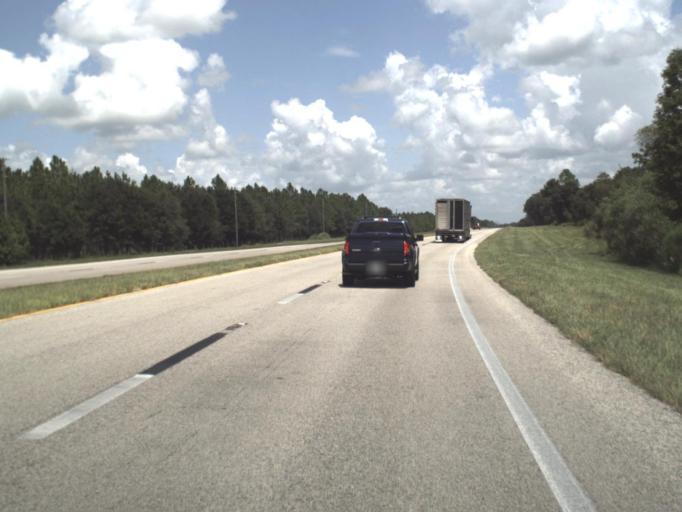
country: US
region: Florida
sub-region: Hardee County
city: Bowling Green
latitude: 27.6943
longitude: -81.8119
